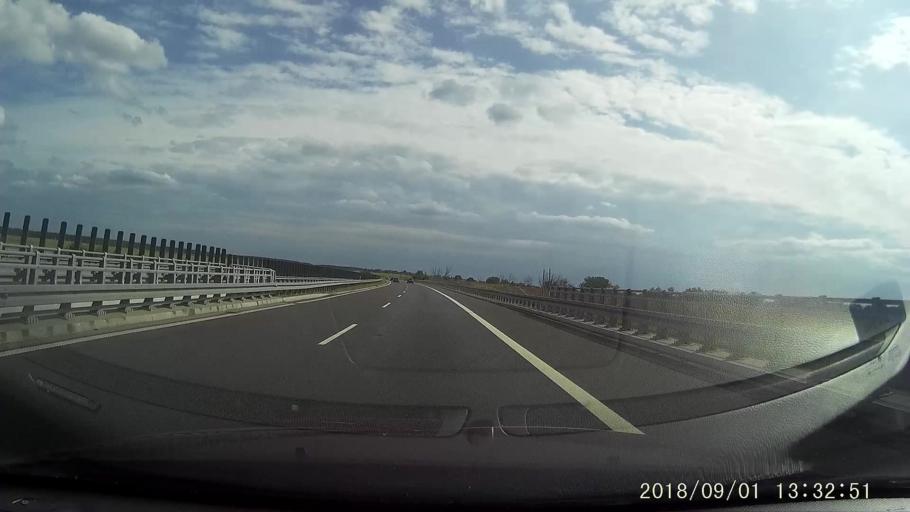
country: PL
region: West Pomeranian Voivodeship
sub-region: Powiat mysliborski
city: Mysliborz
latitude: 52.9901
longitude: 14.8668
